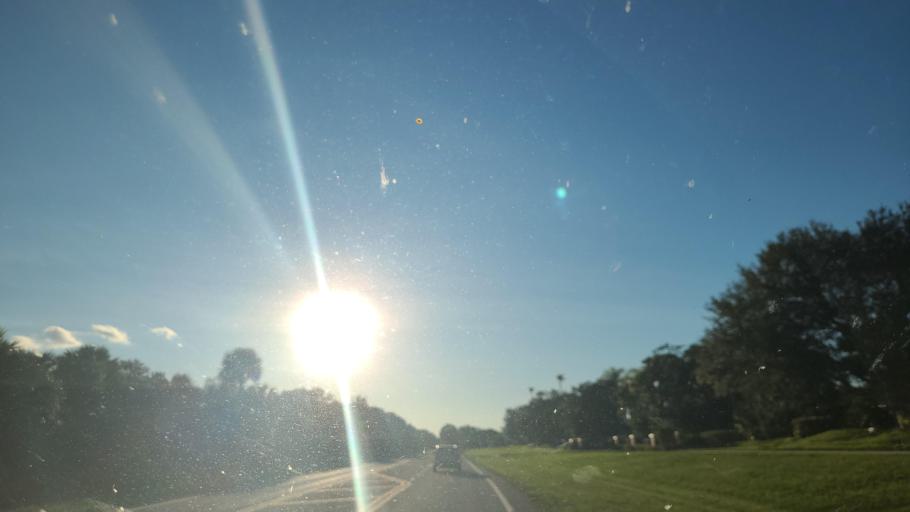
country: US
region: Florida
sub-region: Indian River County
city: Vero Beach South
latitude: 27.6096
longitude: -80.4402
